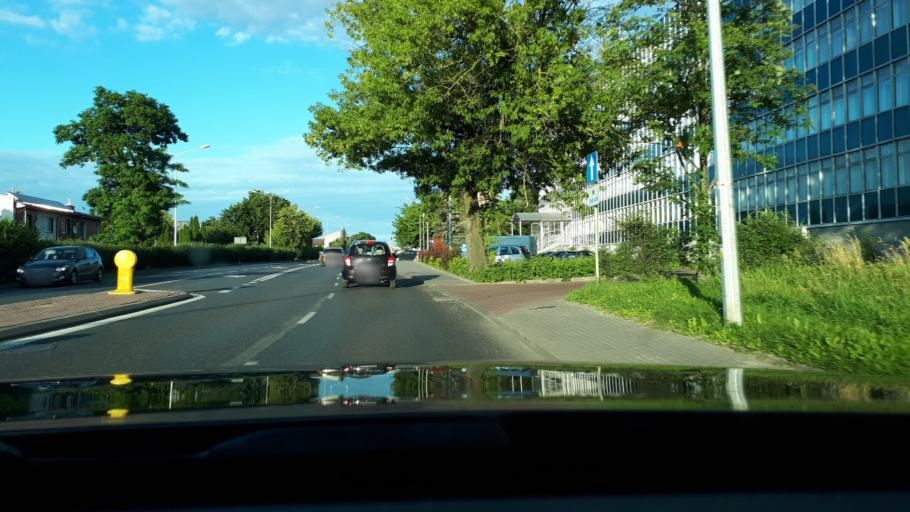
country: PL
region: Masovian Voivodeship
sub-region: Powiat ciechanowski
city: Ciechanow
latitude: 52.8818
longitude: 20.6143
